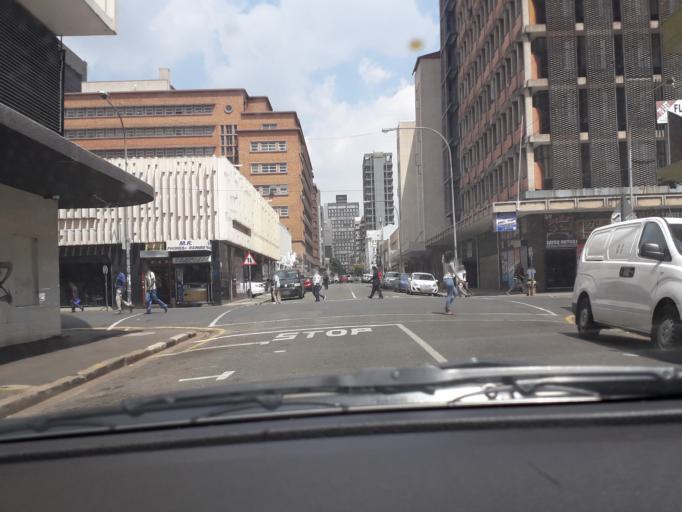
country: ZA
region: Gauteng
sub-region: City of Johannesburg Metropolitan Municipality
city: Johannesburg
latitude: -26.2081
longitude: 28.0447
